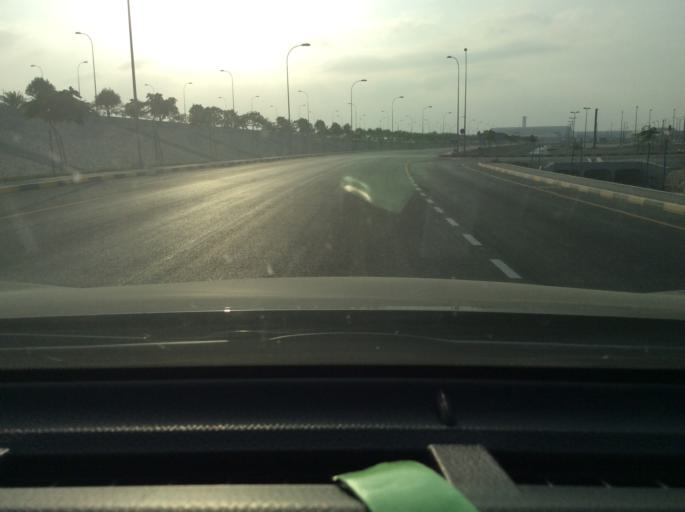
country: OM
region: Muhafazat Masqat
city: Bawshar
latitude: 23.6035
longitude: 58.3082
